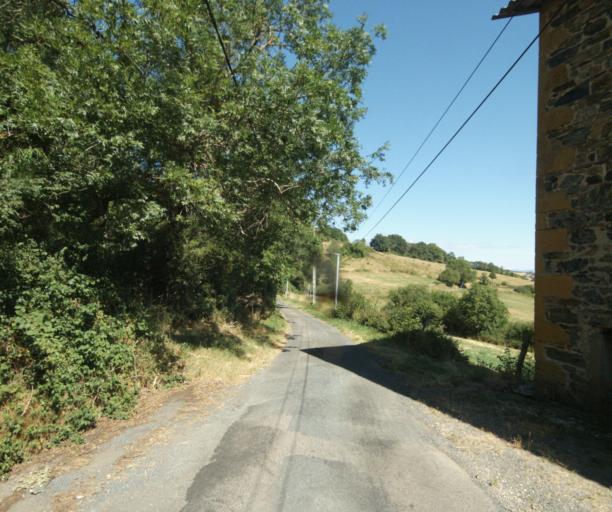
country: FR
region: Rhone-Alpes
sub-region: Departement du Rhone
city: Montrottier
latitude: 45.8103
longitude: 4.4906
